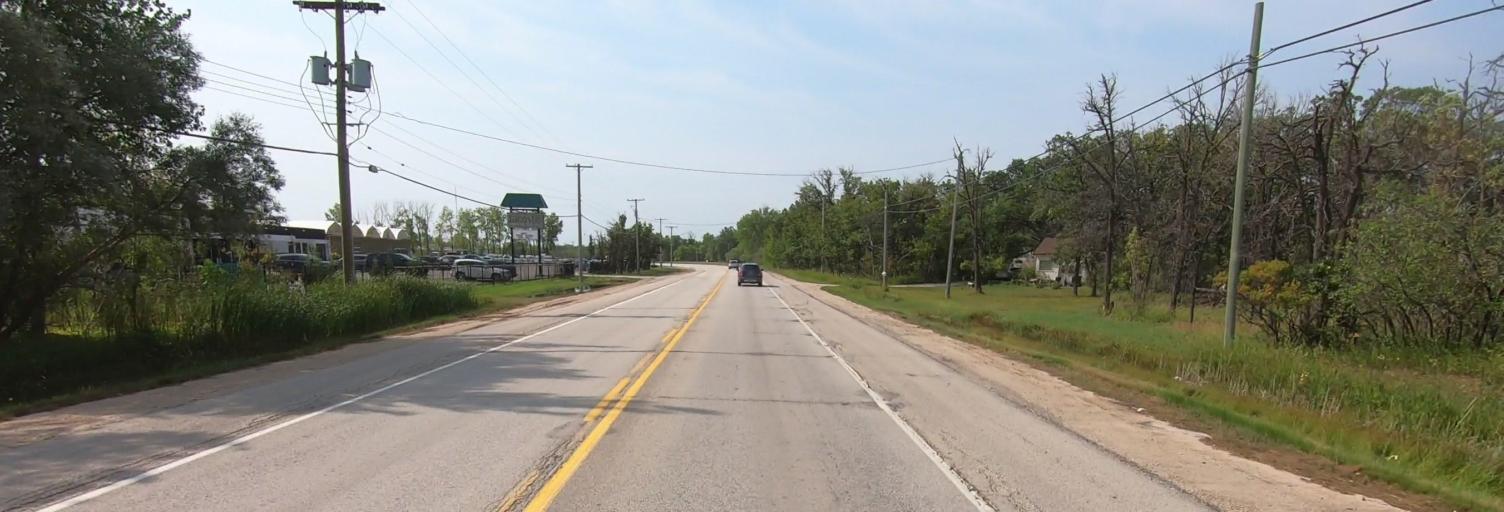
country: CA
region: Manitoba
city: Winnipeg
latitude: 49.7828
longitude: -97.1233
